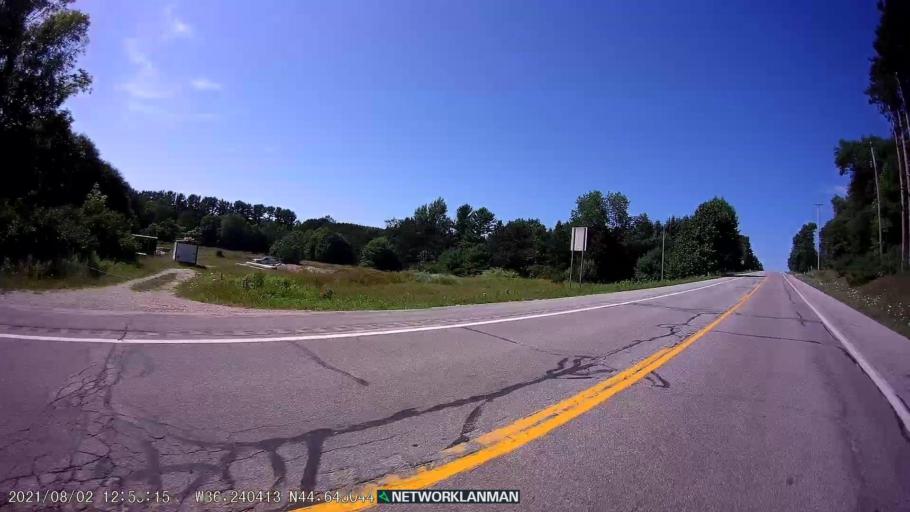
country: US
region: Michigan
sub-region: Benzie County
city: Frankfort
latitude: 44.6454
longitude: -86.2404
